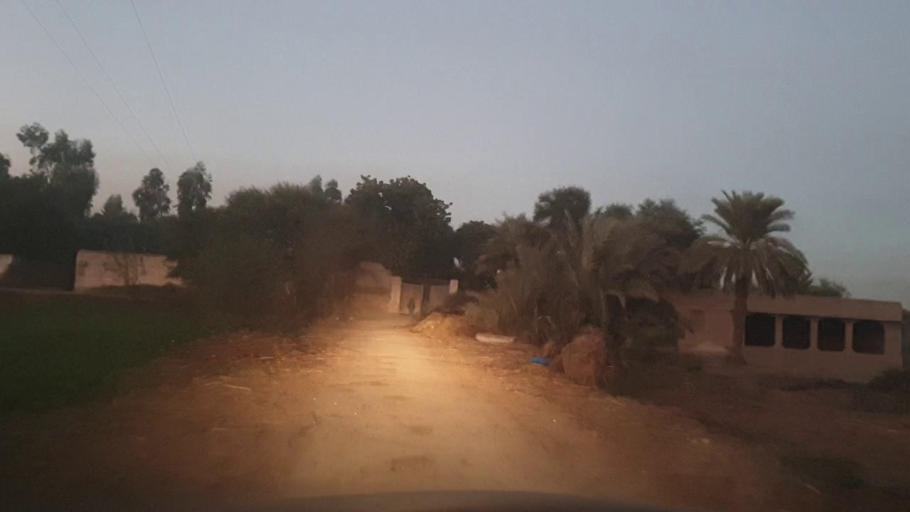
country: PK
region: Sindh
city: Ghotki
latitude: 28.0301
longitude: 69.3611
